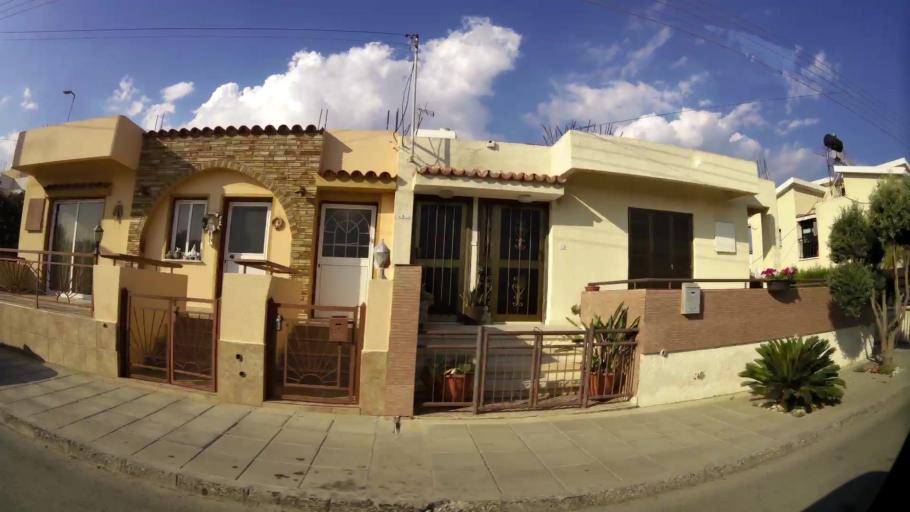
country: CY
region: Larnaka
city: Dhromolaxia
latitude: 34.8758
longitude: 33.5945
